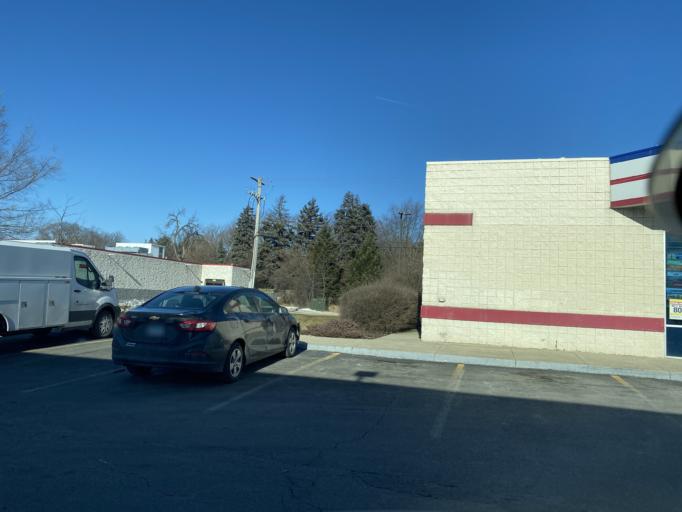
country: US
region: Illinois
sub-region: DuPage County
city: Oakbrook Terrace
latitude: 41.8610
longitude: -87.9711
